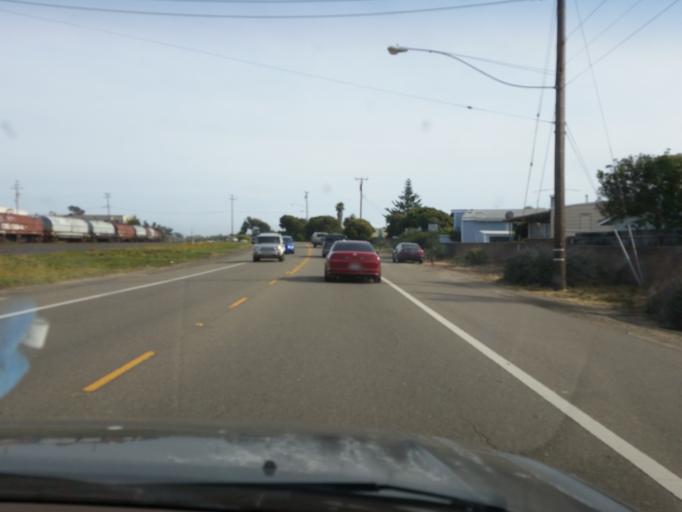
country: US
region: California
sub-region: San Luis Obispo County
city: Grover Beach
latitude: 35.1276
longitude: -120.6319
